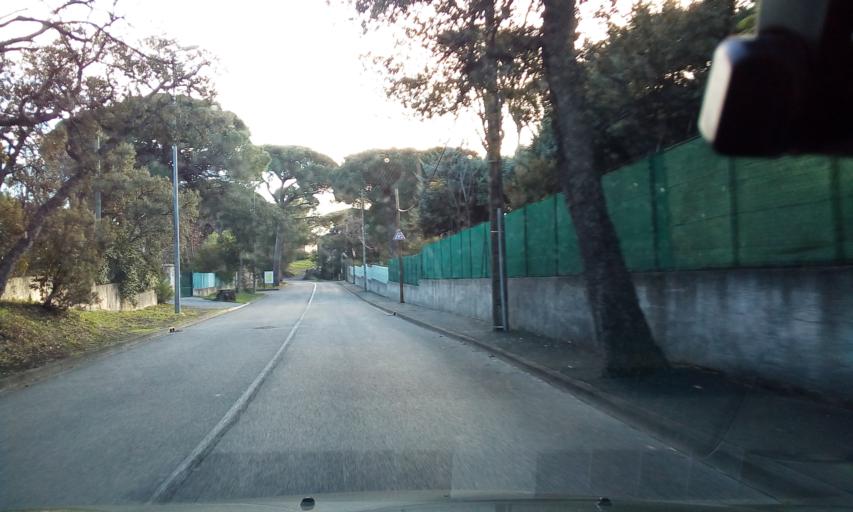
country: FR
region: Provence-Alpes-Cote d'Azur
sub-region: Departement du Var
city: Saint-Raphael
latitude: 43.4422
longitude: 6.7675
